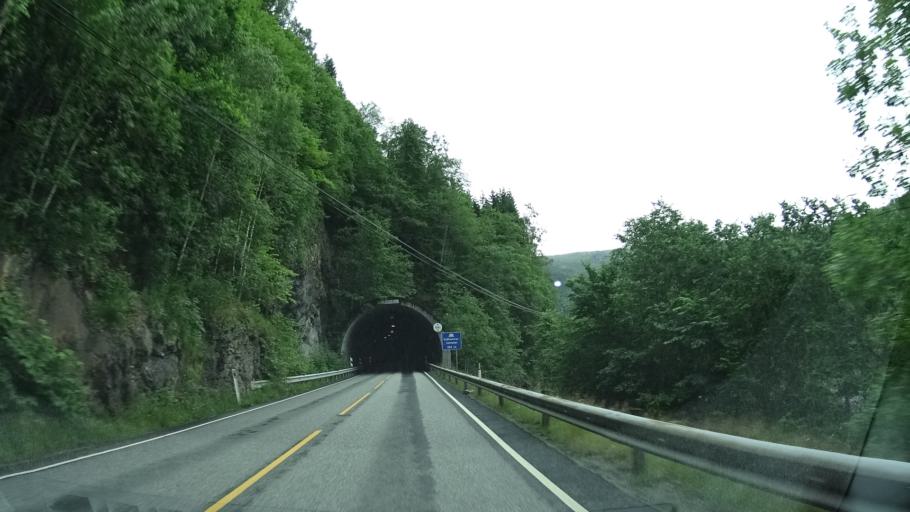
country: NO
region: Hordaland
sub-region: Granvin
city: Granvin
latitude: 60.5388
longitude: 6.7268
